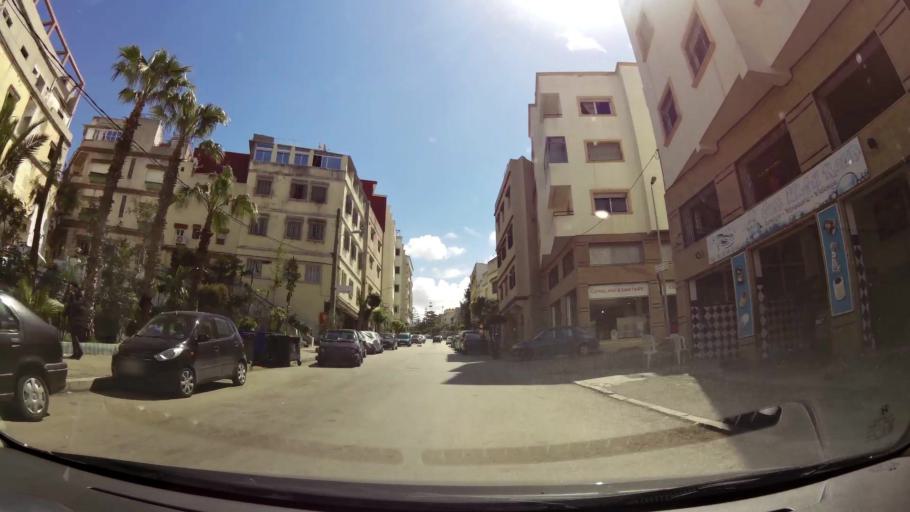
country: MA
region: Tanger-Tetouan
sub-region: Tanger-Assilah
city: Tangier
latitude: 35.7833
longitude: -5.8302
